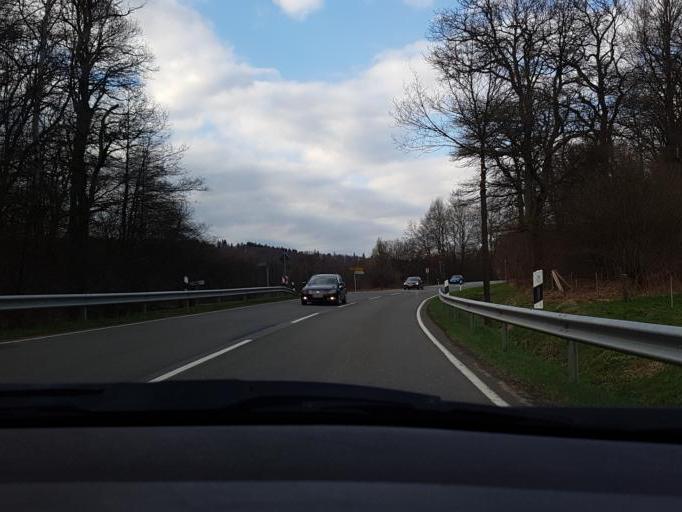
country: DE
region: Lower Saxony
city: Derental
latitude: 51.7278
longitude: 9.5118
